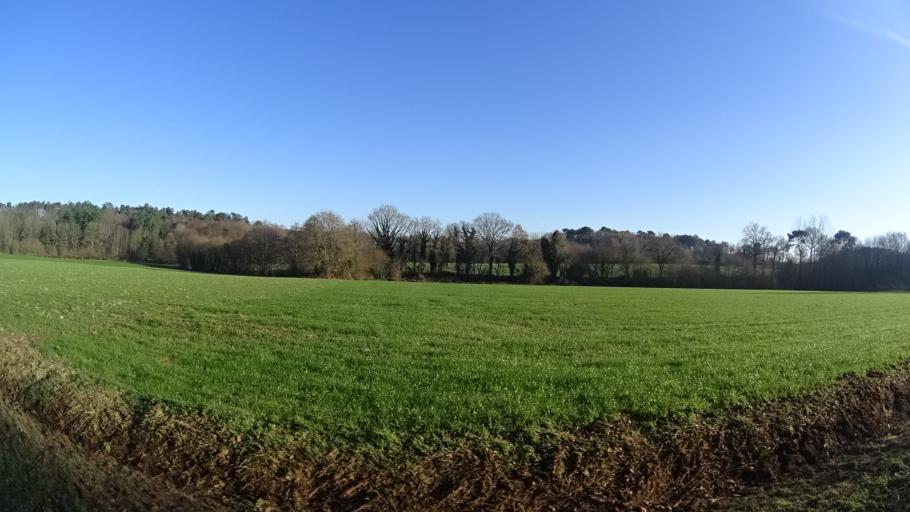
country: FR
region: Brittany
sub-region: Departement du Morbihan
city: Allaire
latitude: 47.6476
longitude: -2.1787
